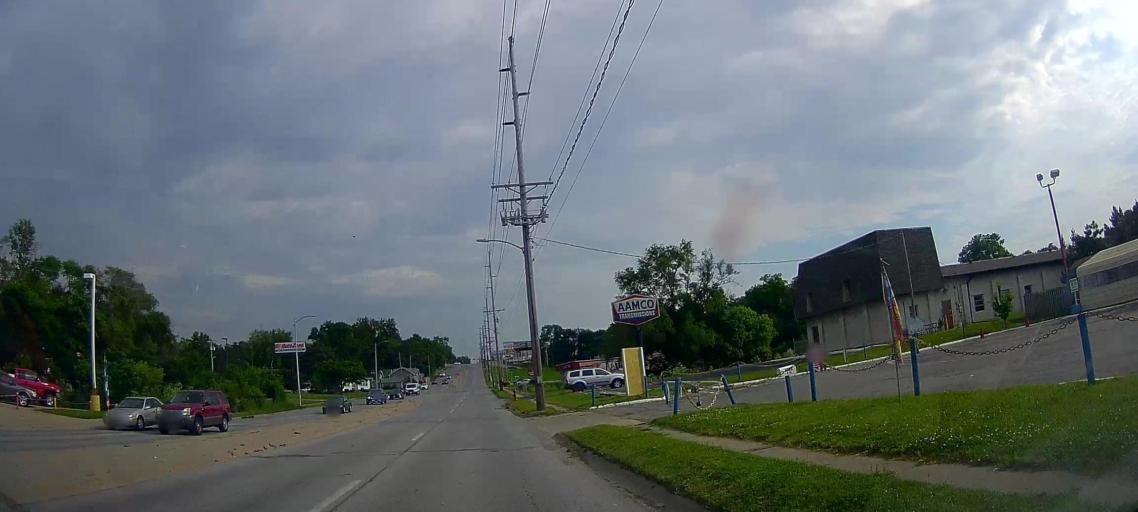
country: US
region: Nebraska
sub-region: Douglas County
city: Ralston
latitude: 41.2898
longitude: -96.0240
